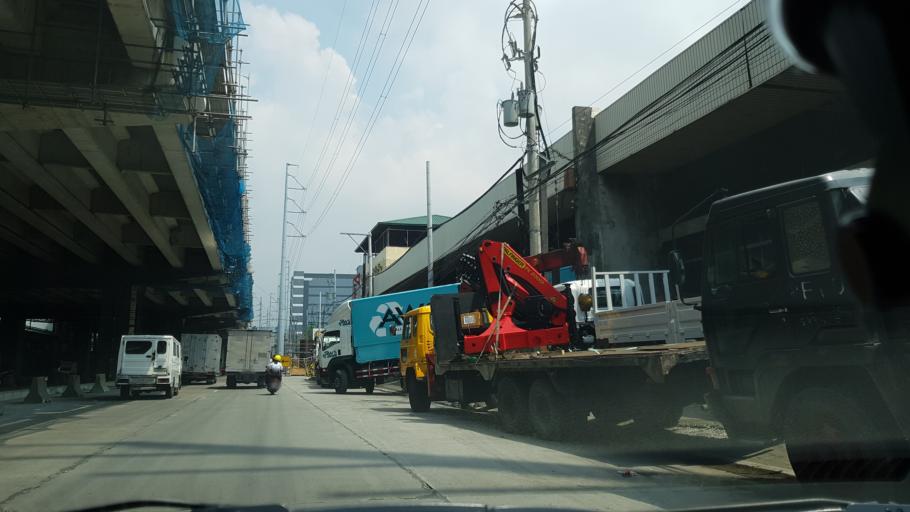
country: PH
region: Metro Manila
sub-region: San Juan
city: San Juan
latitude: 14.6101
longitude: 121.0171
